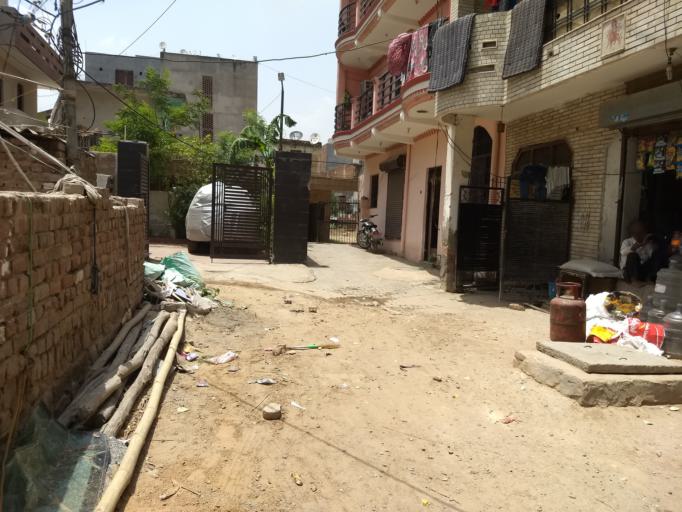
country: IN
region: Haryana
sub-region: Gurgaon
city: Gurgaon
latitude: 28.4898
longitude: 77.1018
